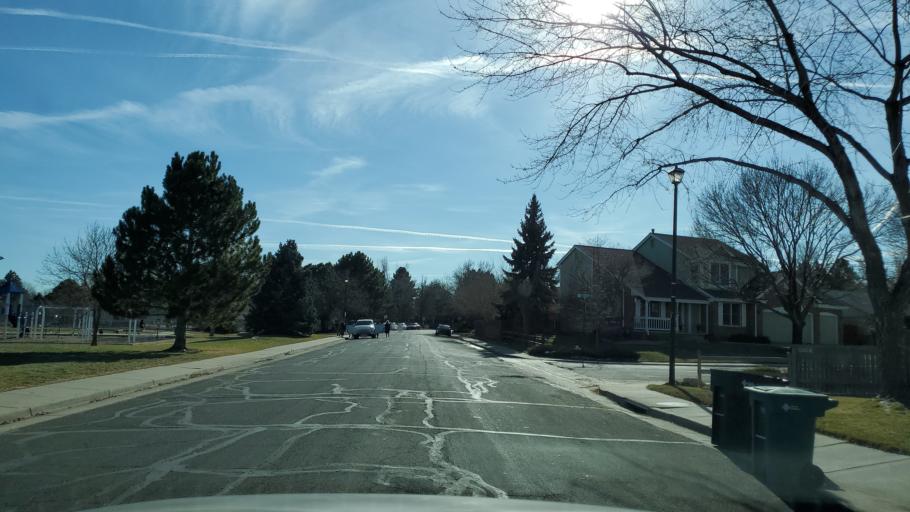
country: US
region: Colorado
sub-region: Adams County
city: Northglenn
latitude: 39.9227
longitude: -104.9527
